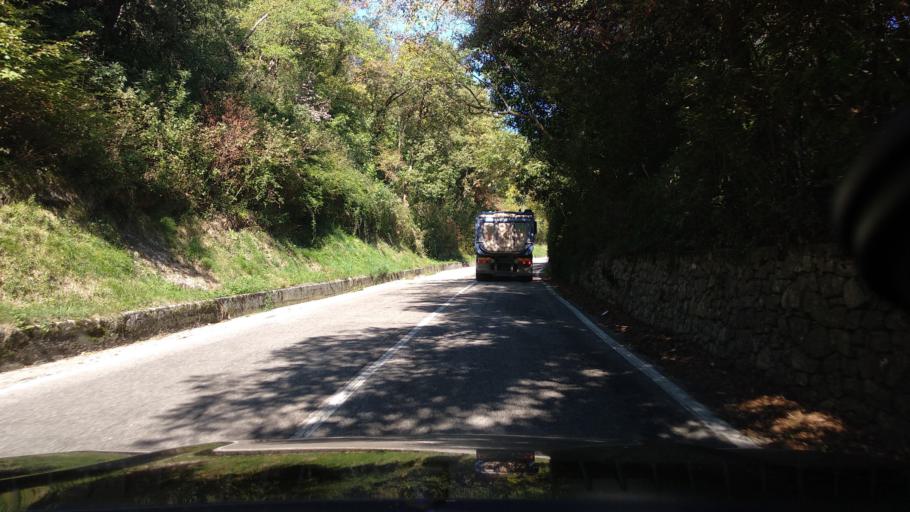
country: IT
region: Veneto
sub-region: Provincia di Verona
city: Garda
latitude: 45.5876
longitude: 10.6993
